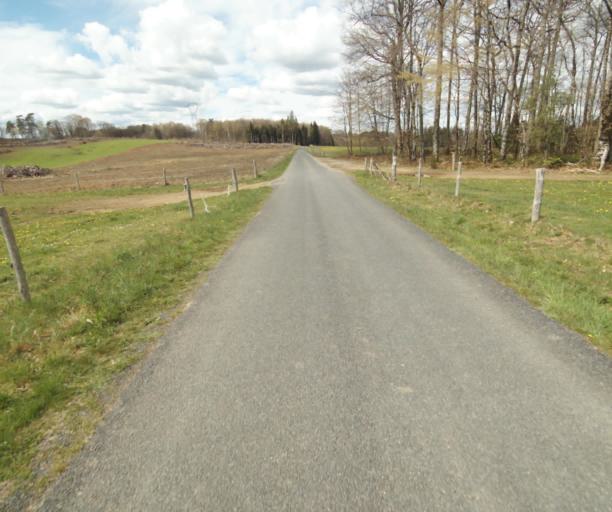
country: FR
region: Limousin
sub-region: Departement de la Correze
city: Argentat
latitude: 45.2030
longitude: 1.9053
